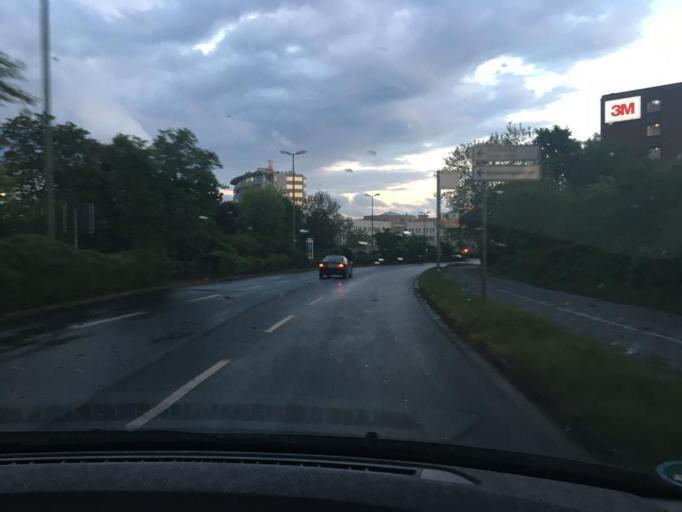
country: DE
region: North Rhine-Westphalia
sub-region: Regierungsbezirk Dusseldorf
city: Neuss
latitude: 51.1976
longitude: 6.7108
